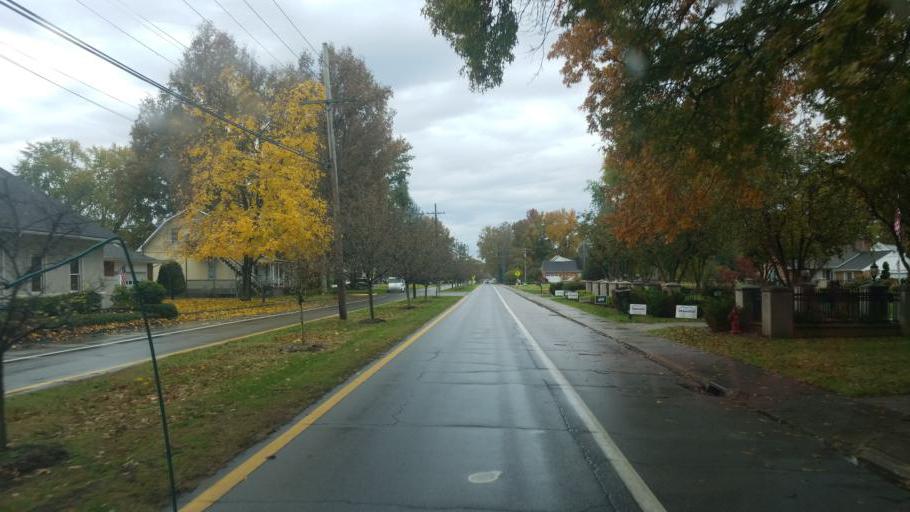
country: US
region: West Virginia
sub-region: Wood County
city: Vienna
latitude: 39.3419
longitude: -81.5392
